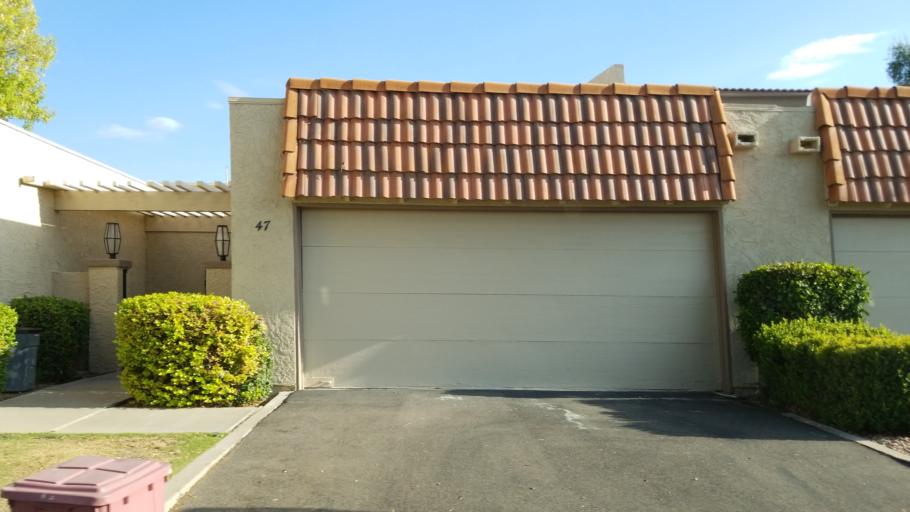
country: US
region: Arizona
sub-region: Maricopa County
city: Scottsdale
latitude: 33.5106
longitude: -111.9181
